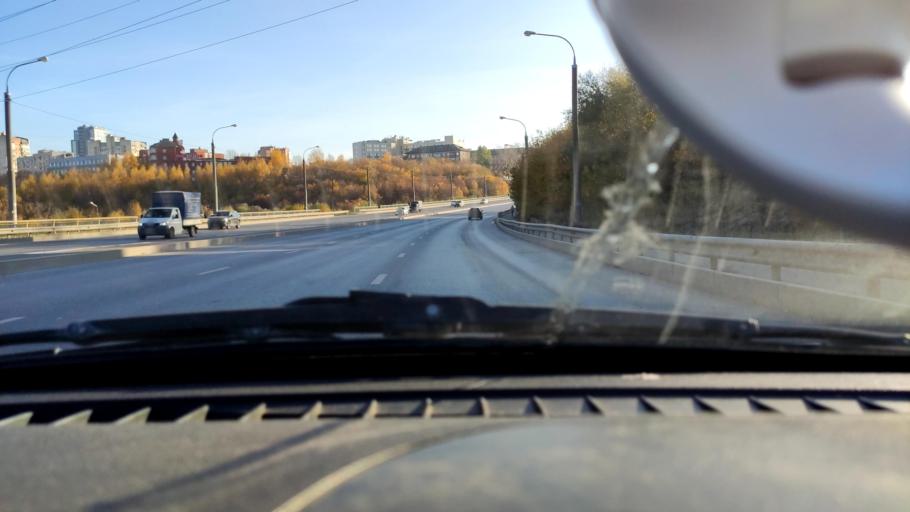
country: RU
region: Perm
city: Perm
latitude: 57.9861
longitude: 56.2337
